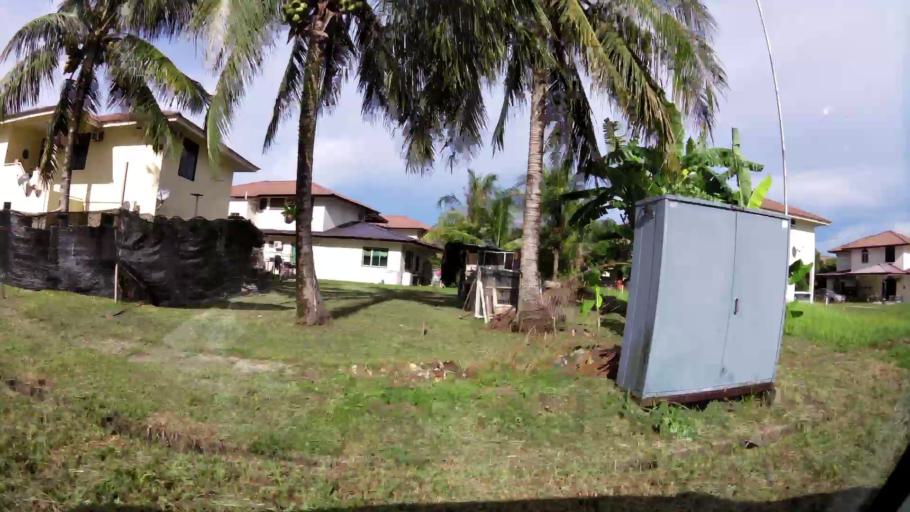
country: BN
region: Brunei and Muara
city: Bandar Seri Begawan
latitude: 4.9689
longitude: 115.0237
